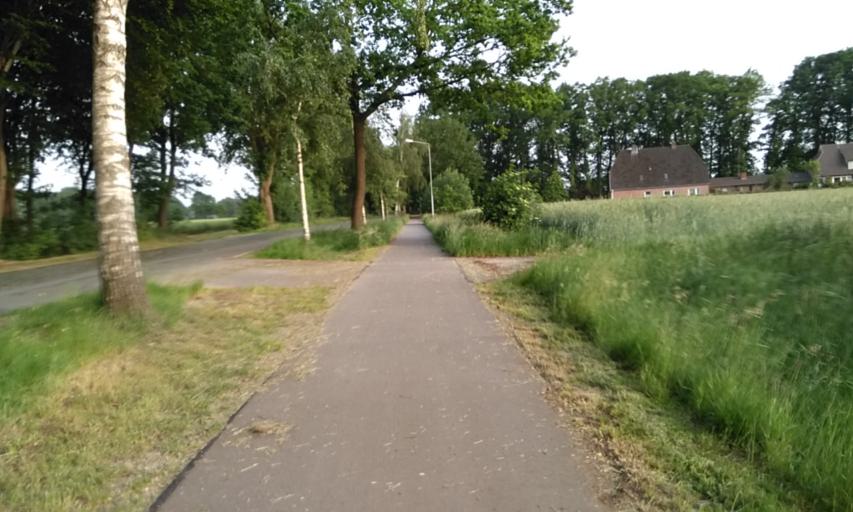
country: DE
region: Lower Saxony
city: Deinste
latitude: 53.5182
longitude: 9.4457
